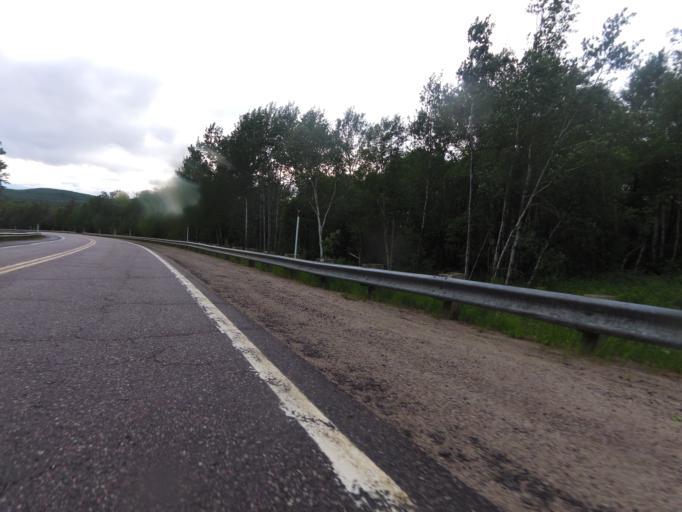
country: CA
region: Quebec
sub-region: Outaouais
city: Shawville
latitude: 45.9080
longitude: -76.2819
